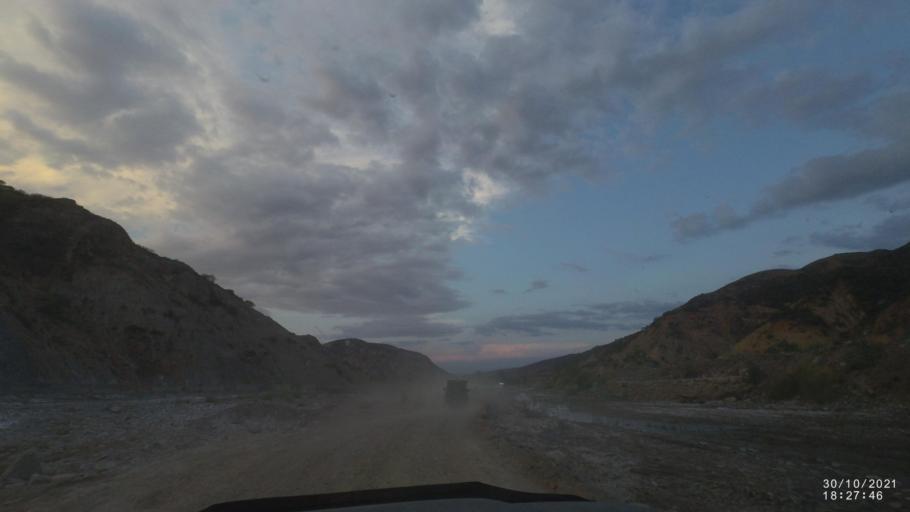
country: BO
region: Cochabamba
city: Sipe Sipe
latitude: -17.5528
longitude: -66.3906
